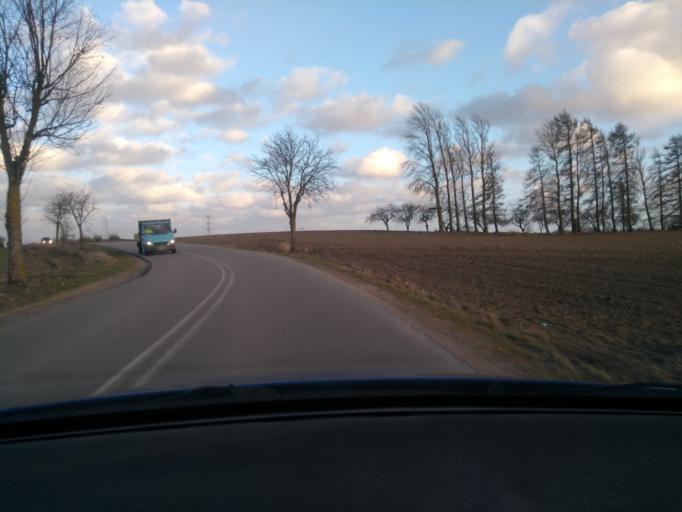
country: PL
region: Pomeranian Voivodeship
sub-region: Powiat kartuski
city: Przodkowo
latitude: 54.4172
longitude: 18.2875
